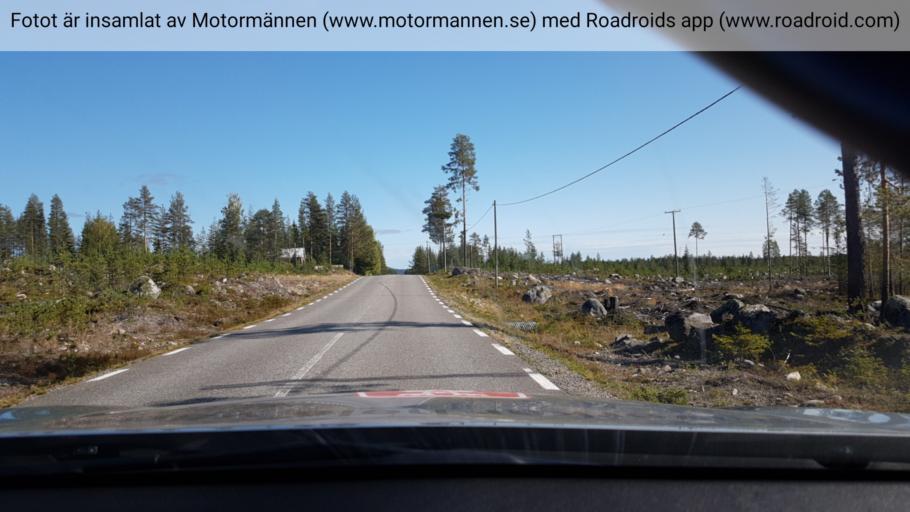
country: SE
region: Vaesterbotten
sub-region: Norsjo Kommun
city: Norsjoe
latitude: 65.1324
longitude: 19.2556
